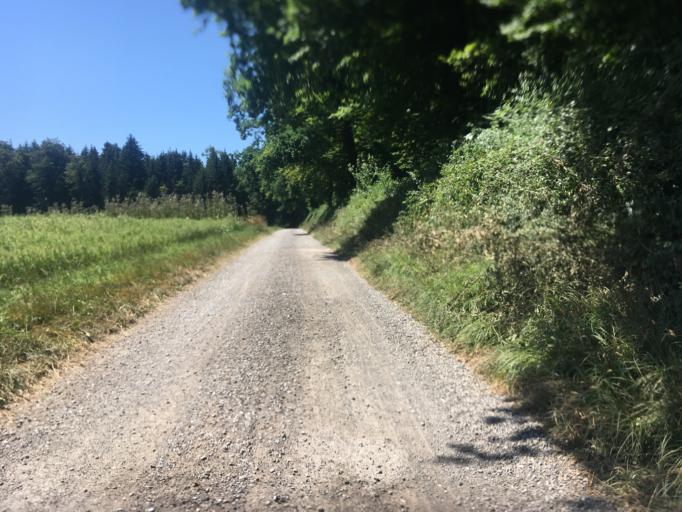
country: CH
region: Solothurn
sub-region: Bezirk Bucheggberg
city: Messen
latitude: 47.0761
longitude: 7.4545
